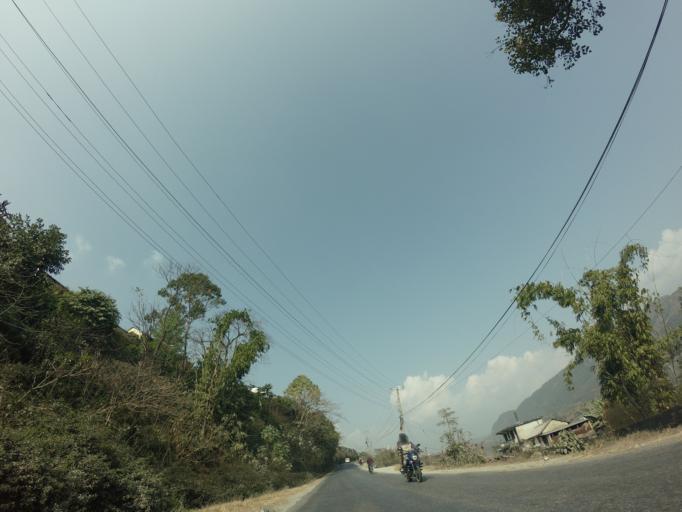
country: NP
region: Western Region
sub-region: Gandaki Zone
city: Pokhara
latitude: 28.2612
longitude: 83.9586
